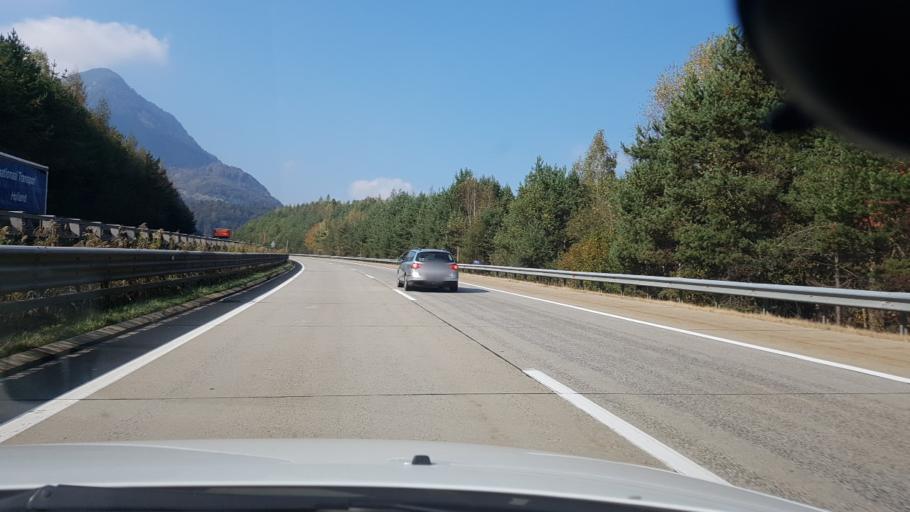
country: AT
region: Carinthia
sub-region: Villach Stadt
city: Villach
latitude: 46.6443
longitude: 13.7930
